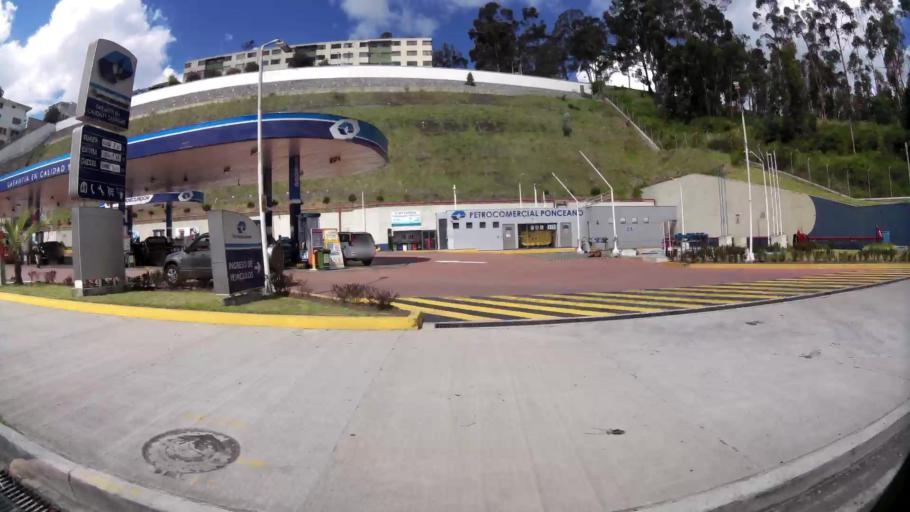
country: EC
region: Pichincha
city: Quito
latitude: -0.0980
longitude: -78.4851
